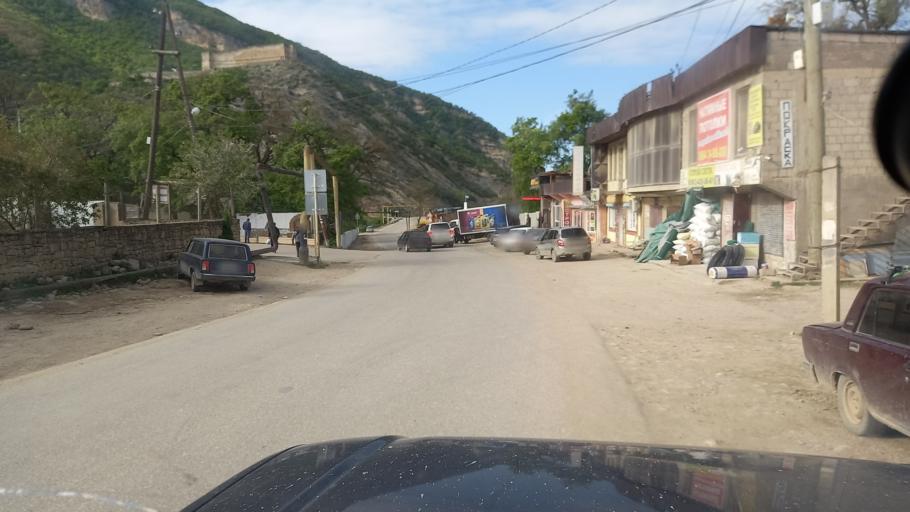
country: RU
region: Dagestan
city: Khuchni
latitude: 41.9614
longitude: 47.9570
